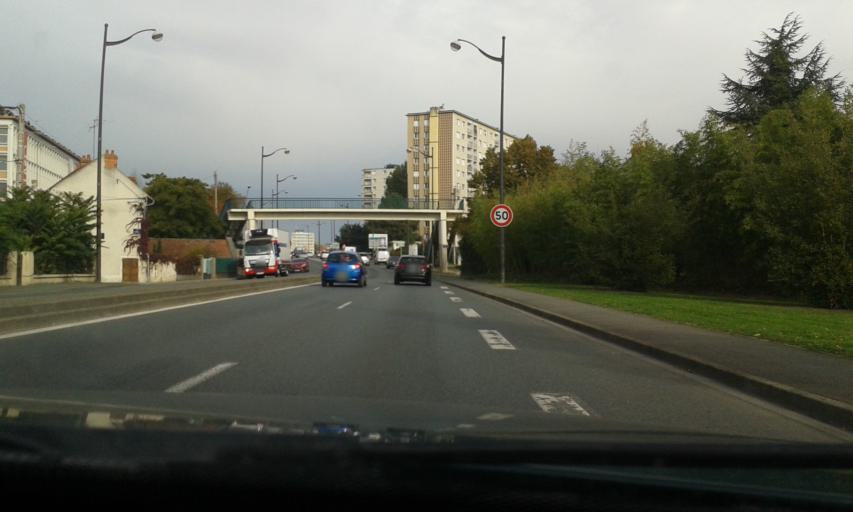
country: FR
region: Centre
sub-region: Departement du Loiret
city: Orleans
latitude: 47.8916
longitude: 1.8957
